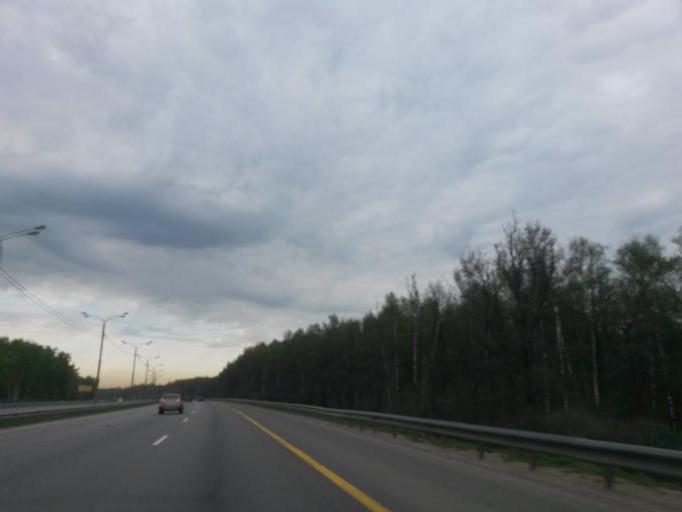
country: RU
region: Moskovskaya
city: Vostryakovo
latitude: 55.3513
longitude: 37.8055
